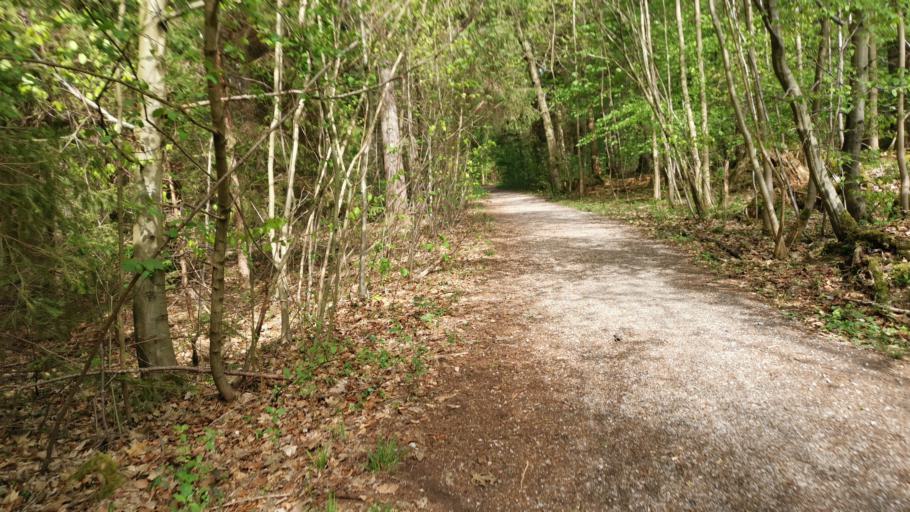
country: DE
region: Bavaria
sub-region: Upper Bavaria
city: Neuried
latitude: 48.0758
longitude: 11.4760
